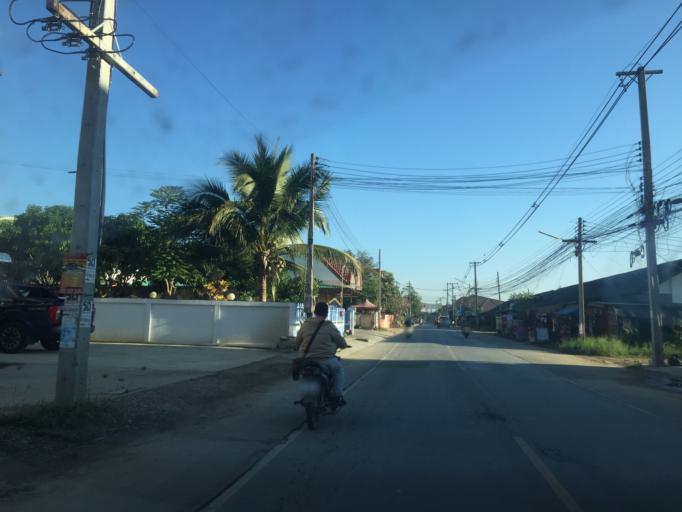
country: TH
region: Lamphun
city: Lamphun
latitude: 18.6046
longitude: 99.0539
